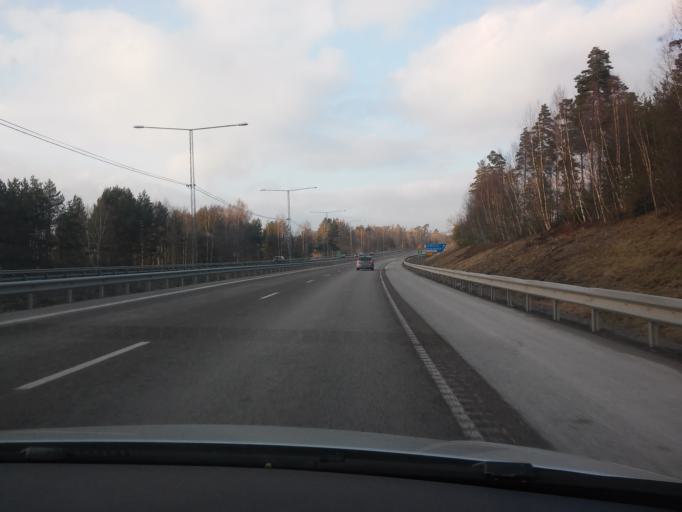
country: SE
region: Stockholm
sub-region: Vallentuna Kommun
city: Vallentuna
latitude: 59.4916
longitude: 18.1642
